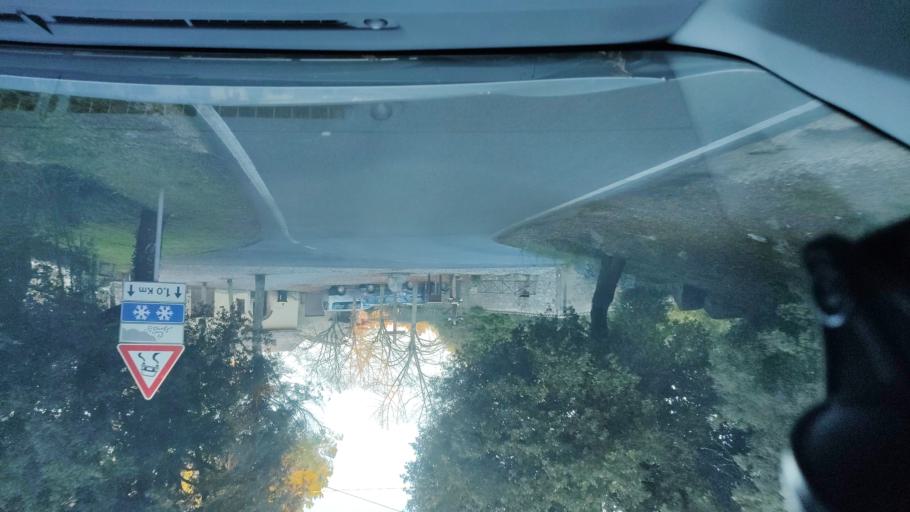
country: IT
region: Umbria
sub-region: Provincia di Terni
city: Amelia
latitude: 42.5836
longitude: 12.4322
